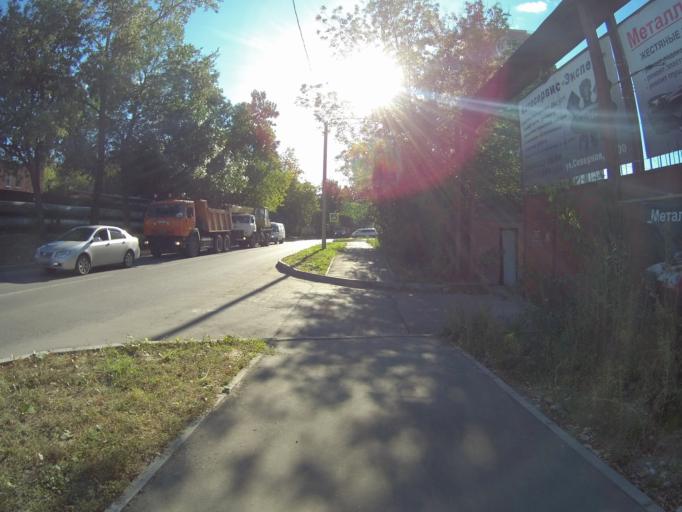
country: RU
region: Vladimir
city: Vladimir
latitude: 56.1438
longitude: 40.3963
